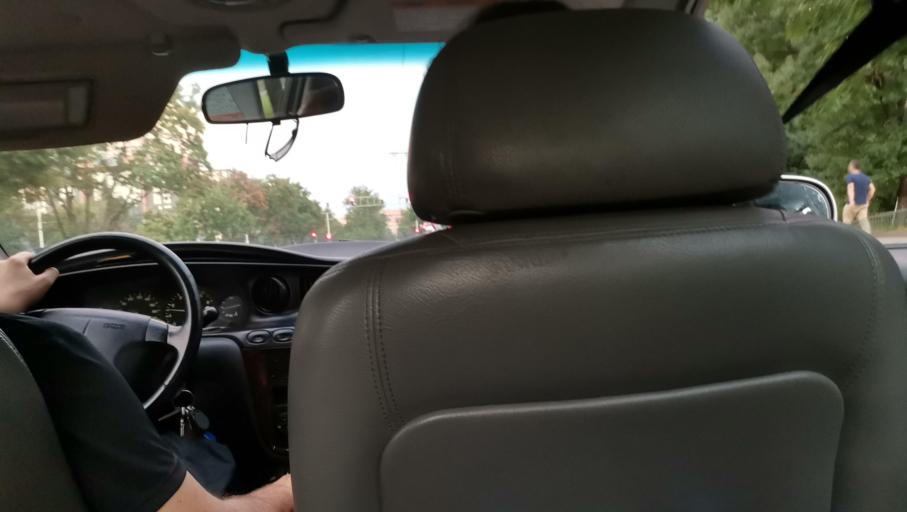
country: BG
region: Plovdiv
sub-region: Obshtina Plovdiv
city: Plovdiv
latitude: 42.1421
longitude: 24.7870
